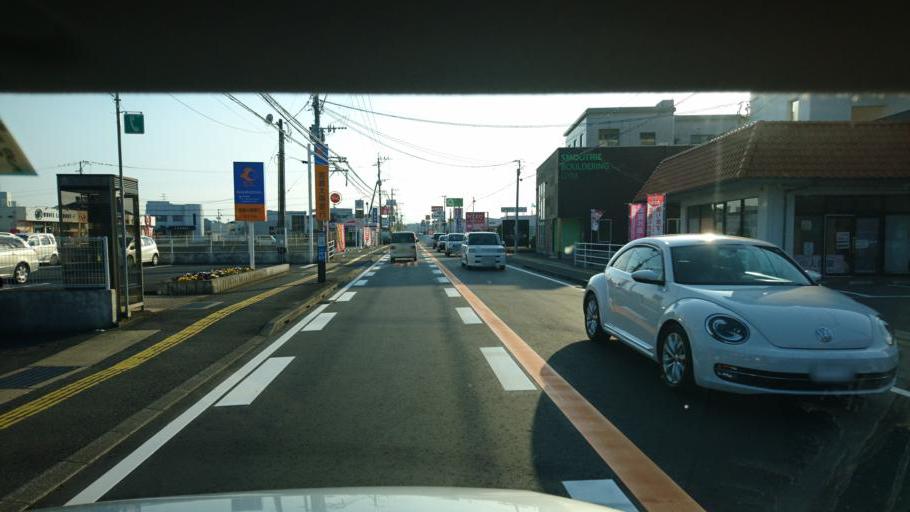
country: JP
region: Miyazaki
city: Miyazaki-shi
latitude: 31.9870
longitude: 131.4510
